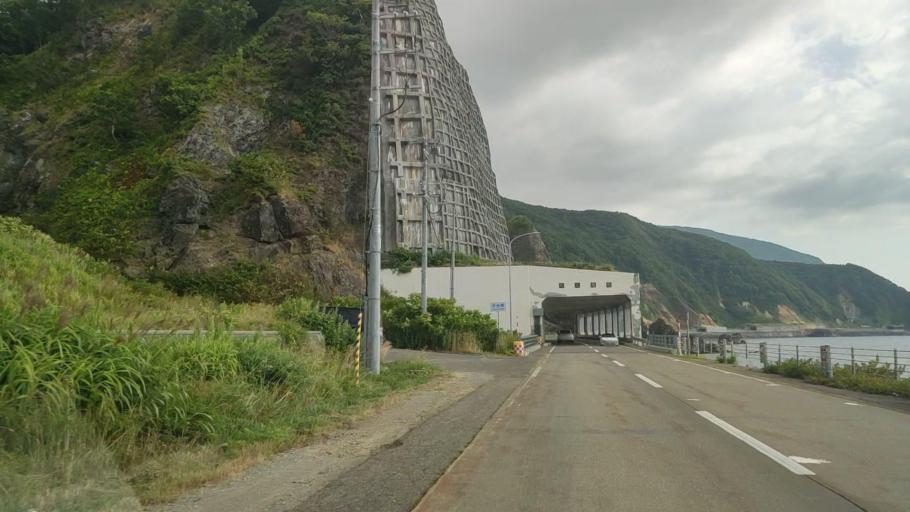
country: JP
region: Hokkaido
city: Rumoi
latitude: 43.7679
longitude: 141.3633
